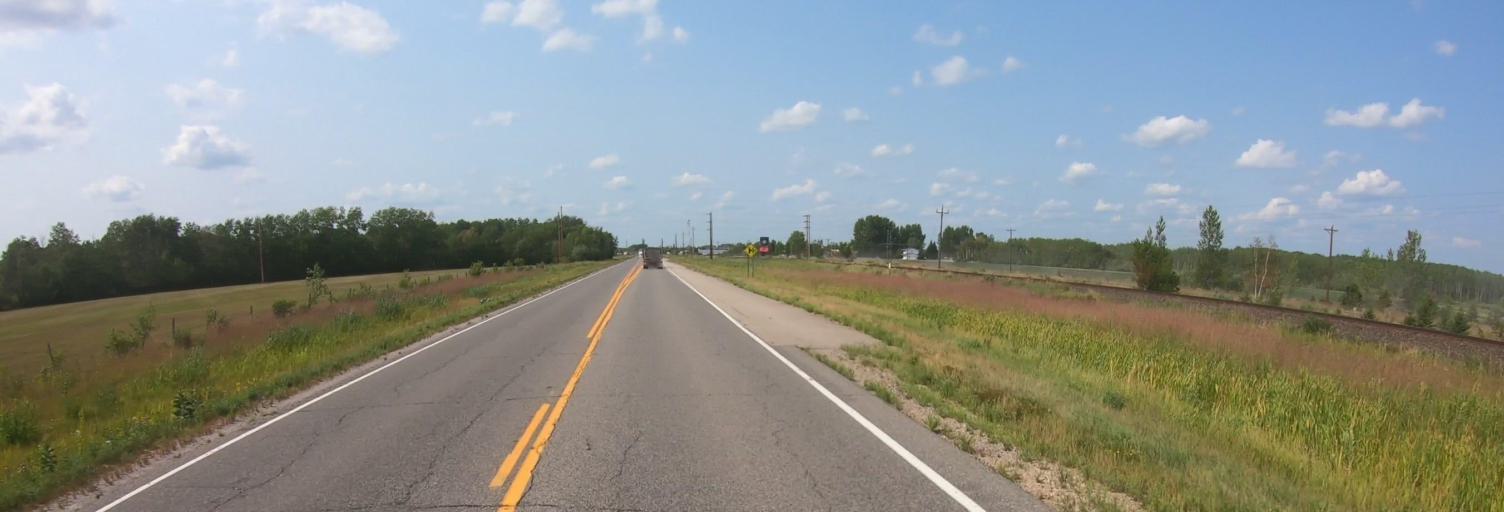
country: US
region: Minnesota
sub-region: Roseau County
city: Warroad
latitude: 48.8908
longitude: -95.3060
